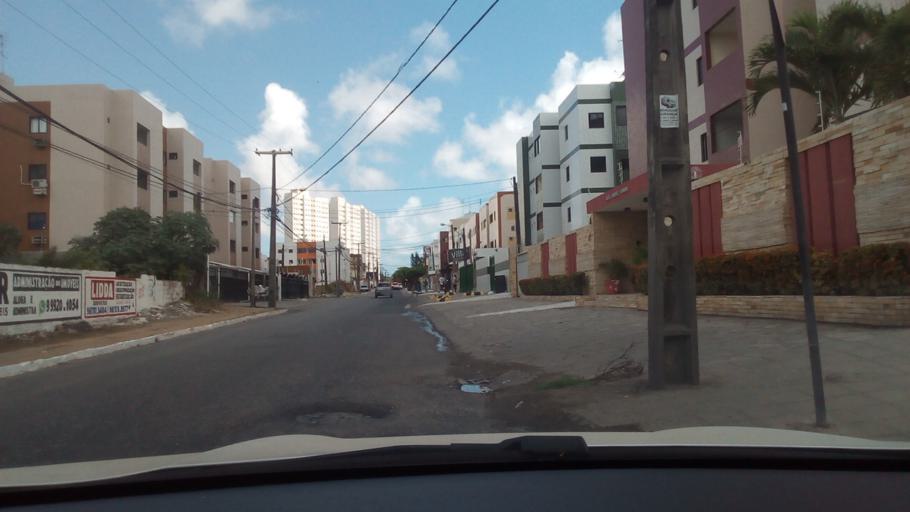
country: BR
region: Paraiba
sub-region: Joao Pessoa
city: Joao Pessoa
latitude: -7.1542
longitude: -34.8521
